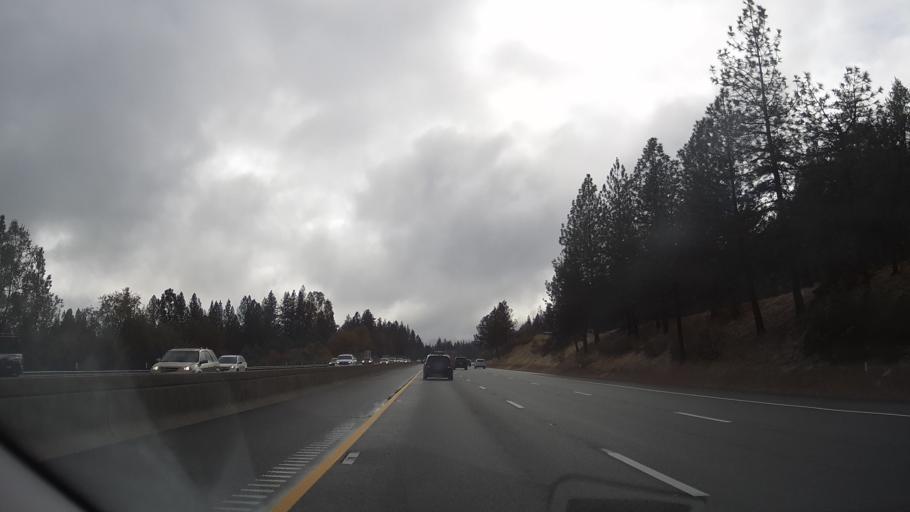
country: US
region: California
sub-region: Placer County
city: Meadow Vista
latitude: 38.9982
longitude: -120.9968
